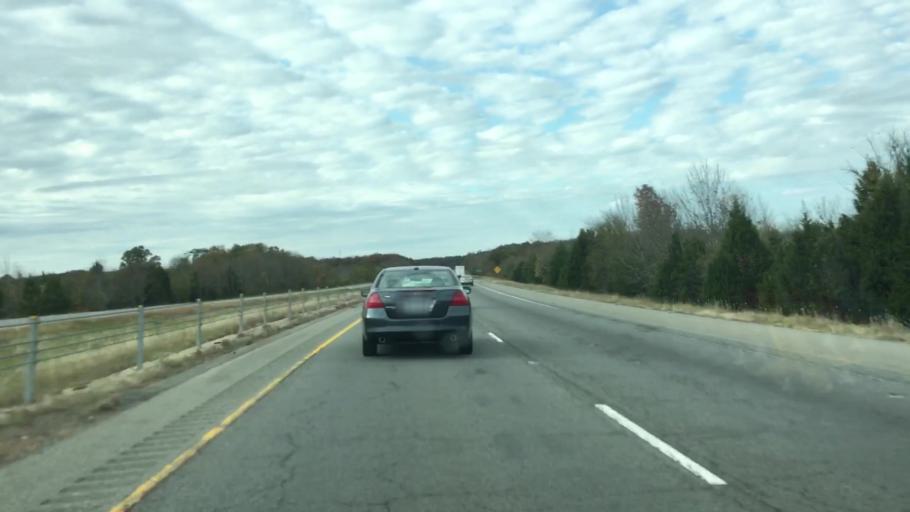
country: US
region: Arkansas
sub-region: Faulkner County
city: Conway
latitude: 35.1275
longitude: -92.5117
